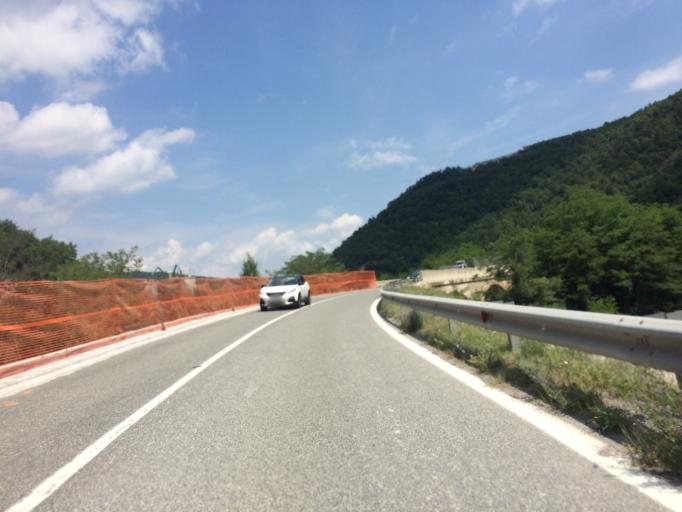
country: IT
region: Piedmont
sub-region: Provincia di Cuneo
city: Bagnasco
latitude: 44.2785
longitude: 8.0345
